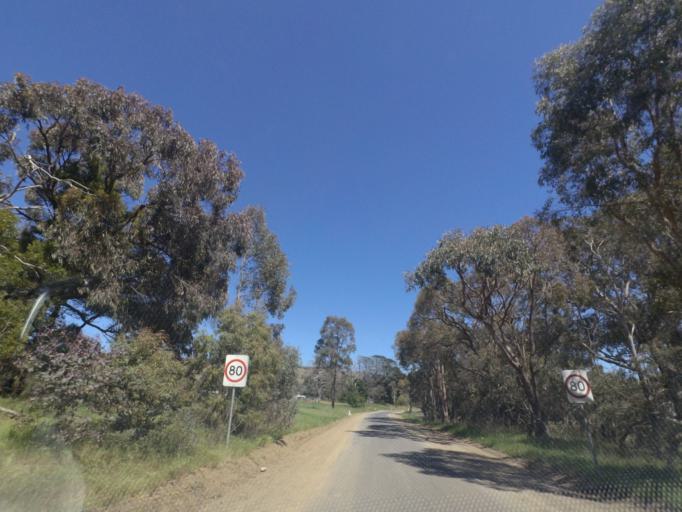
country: AU
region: Victoria
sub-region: Whittlesea
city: Whittlesea
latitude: -37.2901
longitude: 144.9888
